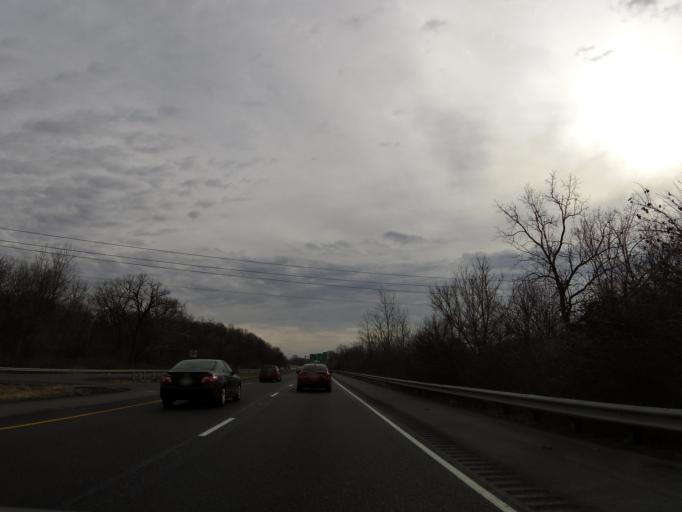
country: US
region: Indiana
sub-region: Marion County
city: Speedway
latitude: 39.8134
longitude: -86.2916
